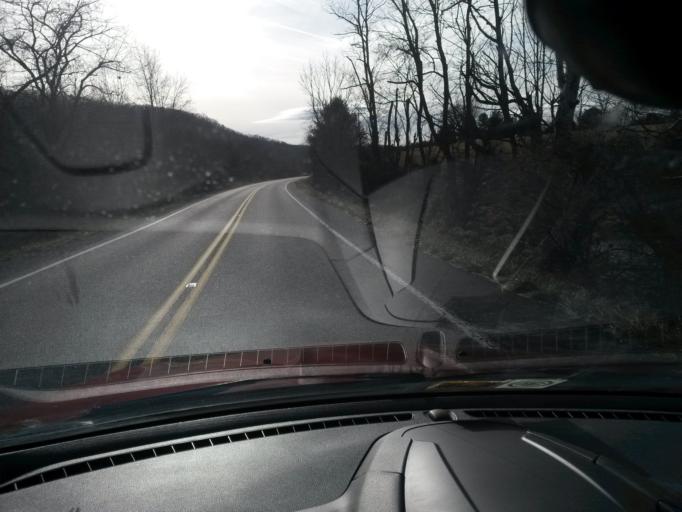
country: US
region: Virginia
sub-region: Augusta County
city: Jolivue
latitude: 38.1012
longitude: -79.3232
